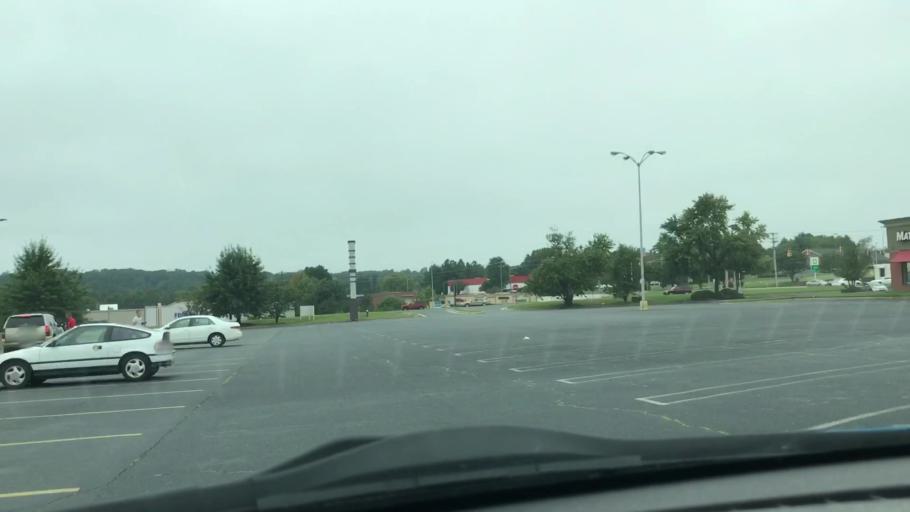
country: US
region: North Carolina
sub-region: Randolph County
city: Asheboro
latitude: 35.6969
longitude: -79.7871
